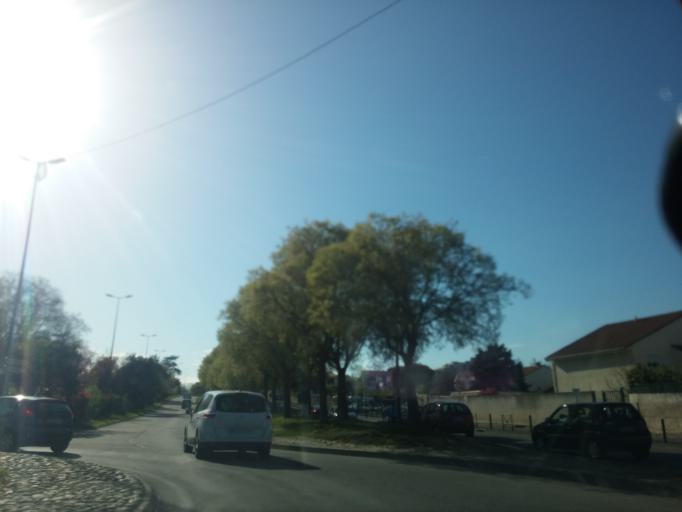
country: FR
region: Midi-Pyrenees
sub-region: Departement de la Haute-Garonne
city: Portet-sur-Garonne
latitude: 43.5744
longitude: 1.4011
